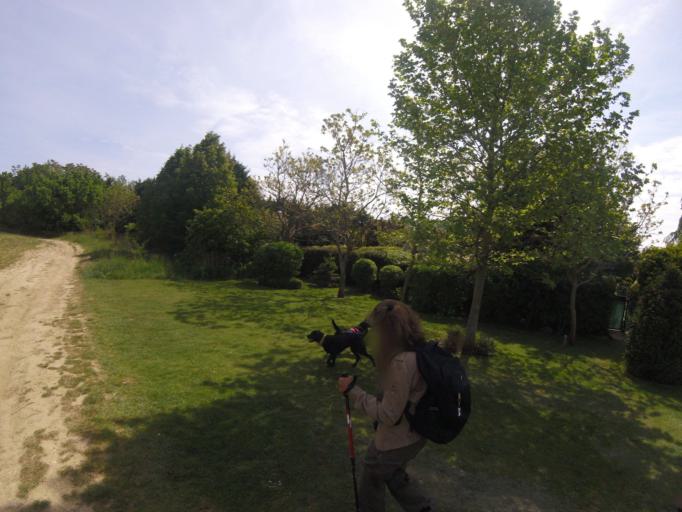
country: HU
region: Pest
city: Telki
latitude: 47.5599
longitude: 18.8231
